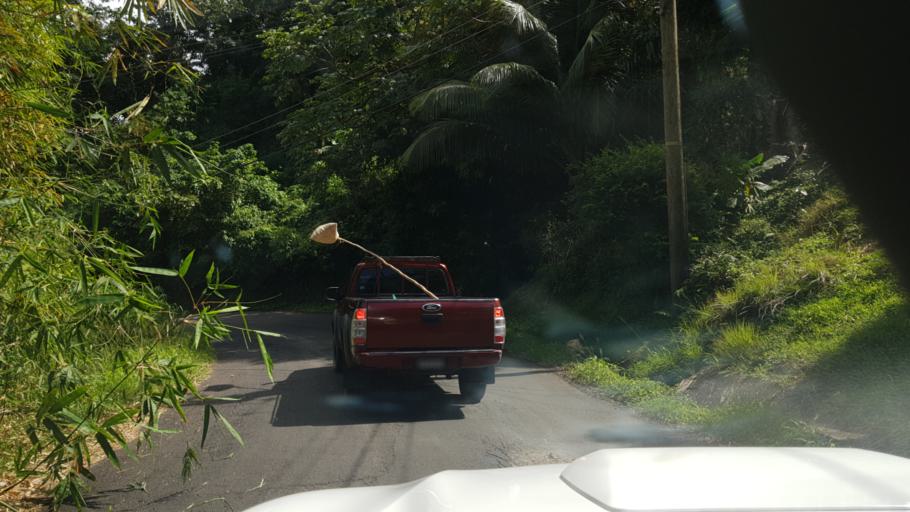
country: LC
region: Castries Quarter
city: Bisee
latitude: 14.0142
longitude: -60.9624
